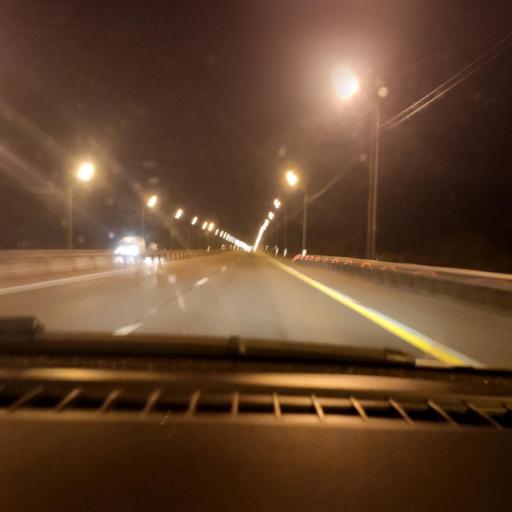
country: RU
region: Lipetsk
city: Khlevnoye
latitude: 52.1920
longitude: 39.1770
